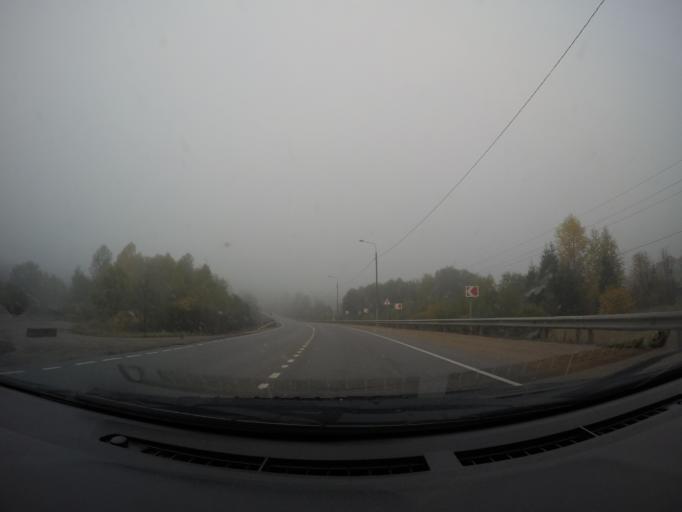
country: RU
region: Moskovskaya
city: Ruza
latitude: 55.7297
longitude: 36.3065
